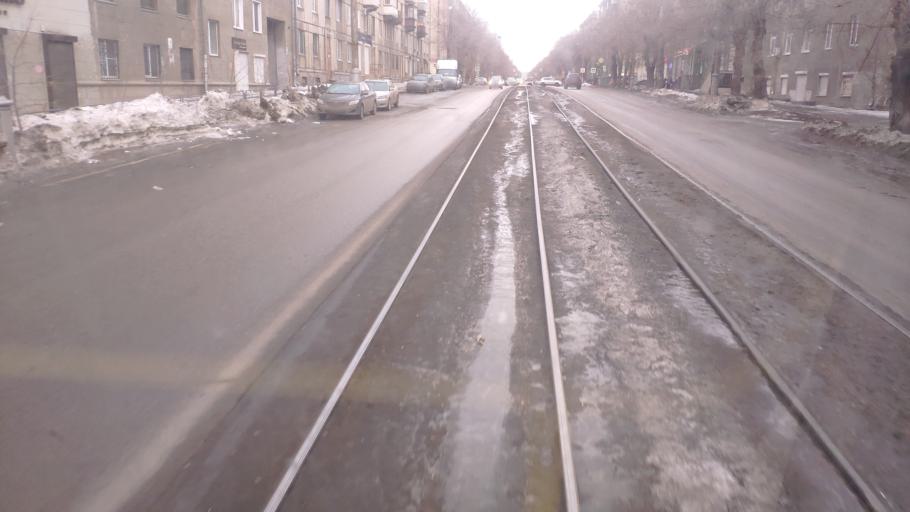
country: RU
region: Chelyabinsk
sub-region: Gorod Magnitogorsk
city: Magnitogorsk
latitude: 53.4177
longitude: 58.9950
